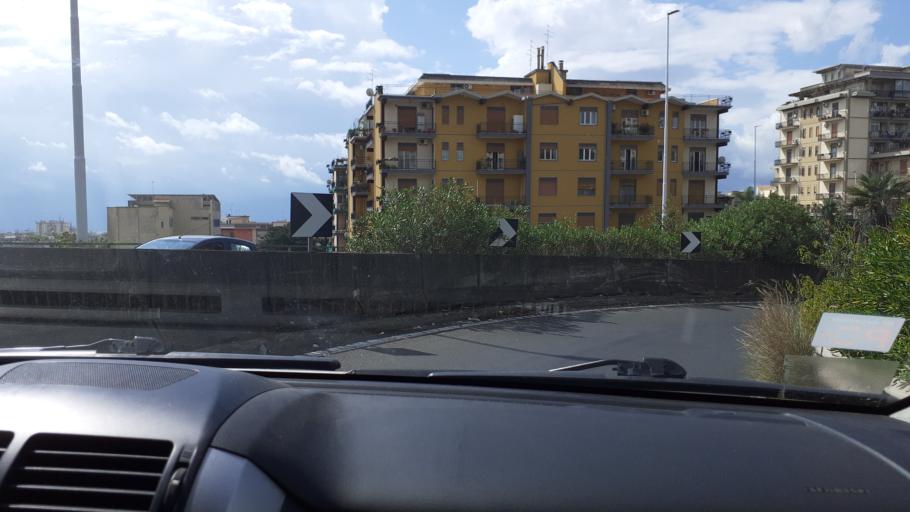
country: IT
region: Sicily
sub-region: Catania
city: Canalicchio
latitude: 37.5273
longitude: 15.0912
